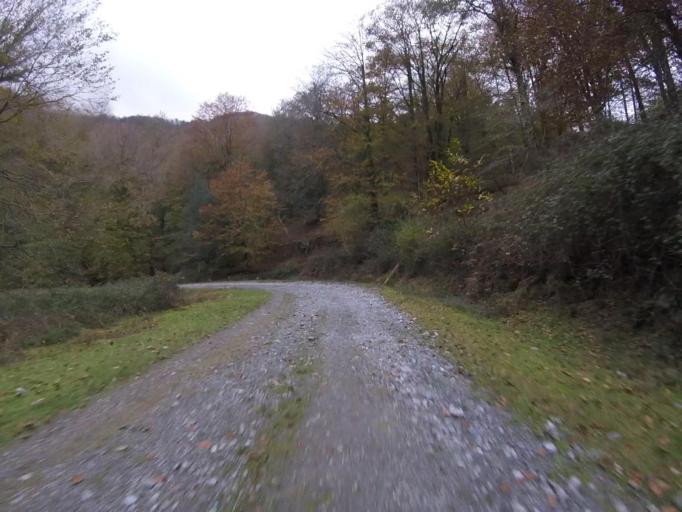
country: ES
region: Navarre
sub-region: Provincia de Navarra
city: Goizueta
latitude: 43.1783
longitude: -1.8058
